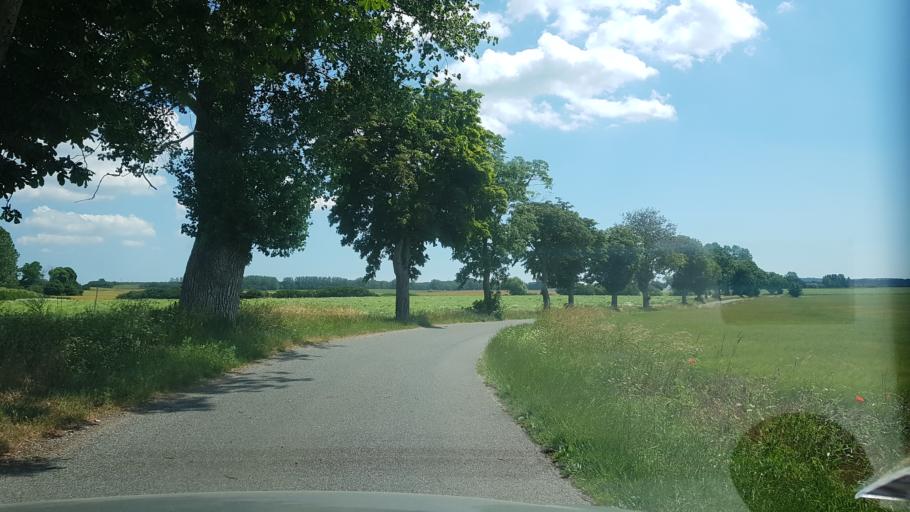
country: DK
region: Zealand
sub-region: Kalundborg Kommune
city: Svebolle
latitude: 55.7056
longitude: 11.2836
